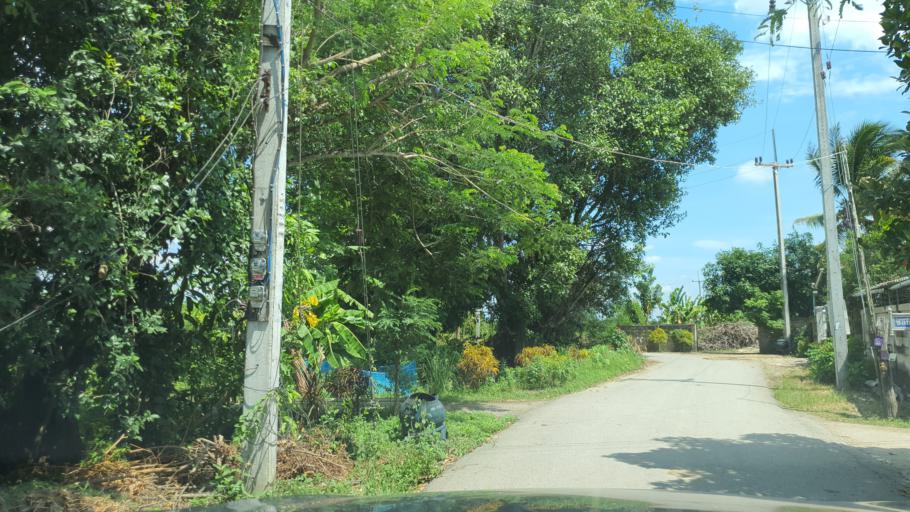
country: TH
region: Chiang Mai
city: Mae Taeng
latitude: 19.0722
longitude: 98.9549
